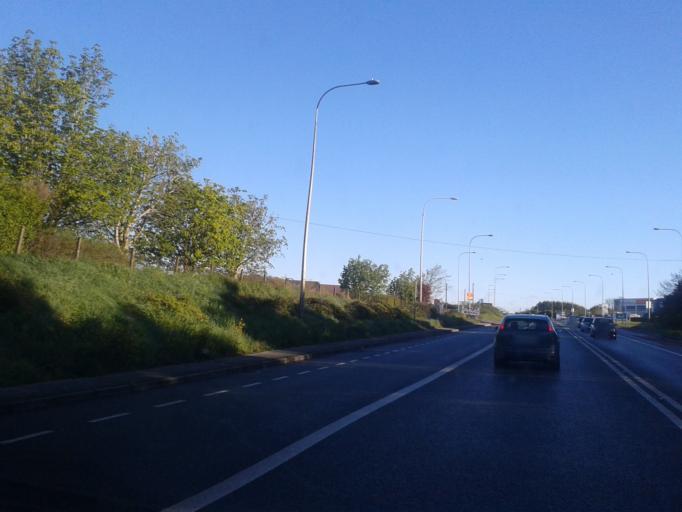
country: IE
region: Leinster
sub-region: Fingal County
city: Swords
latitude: 53.4403
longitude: -6.2277
